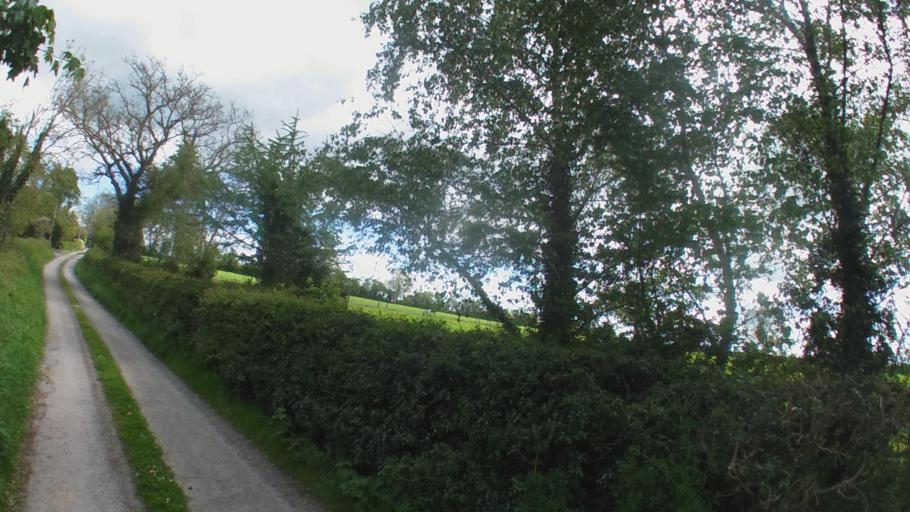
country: IE
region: Leinster
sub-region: Kilkenny
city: Thomastown
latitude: 52.6002
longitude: -7.1723
